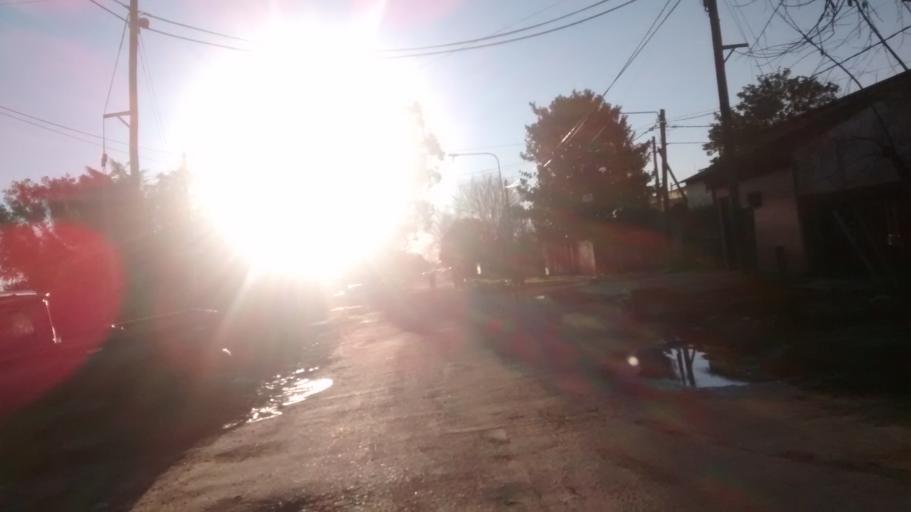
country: AR
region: Buenos Aires
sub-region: Partido de La Plata
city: La Plata
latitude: -34.9622
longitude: -57.9408
